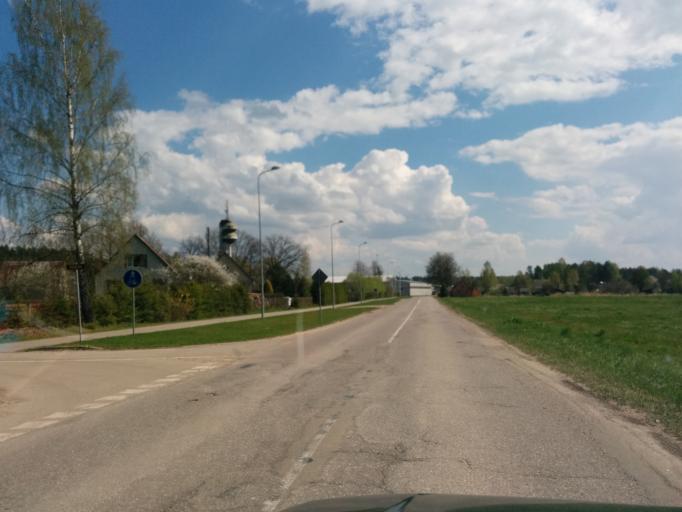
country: LV
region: Jelgava
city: Jelgava
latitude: 56.6185
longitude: 23.7743
